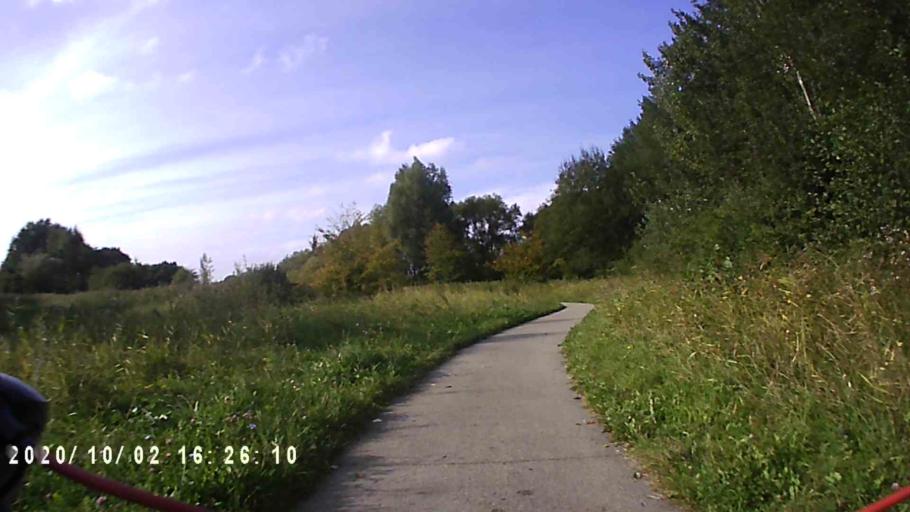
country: NL
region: Groningen
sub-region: Gemeente Zuidhorn
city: Grijpskerk
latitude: 53.2855
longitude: 6.3122
